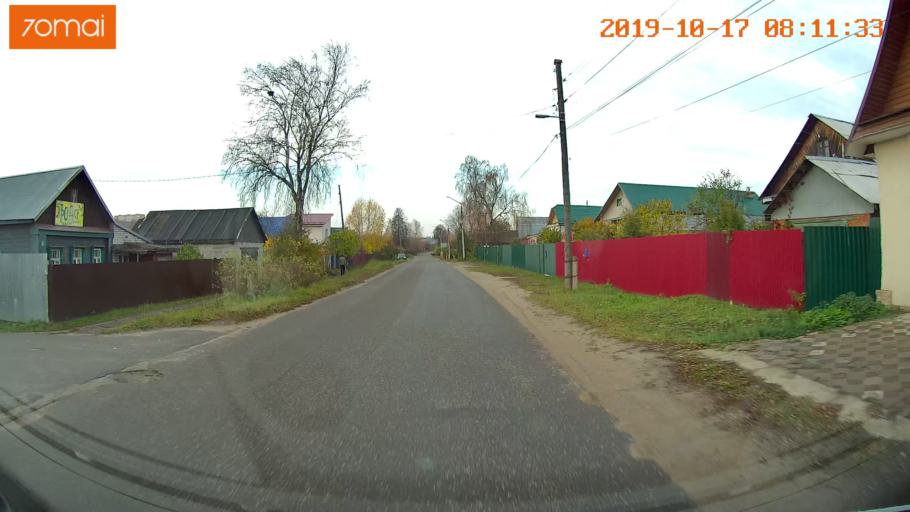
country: RU
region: Vladimir
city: Kol'chugino
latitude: 56.3025
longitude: 39.3679
